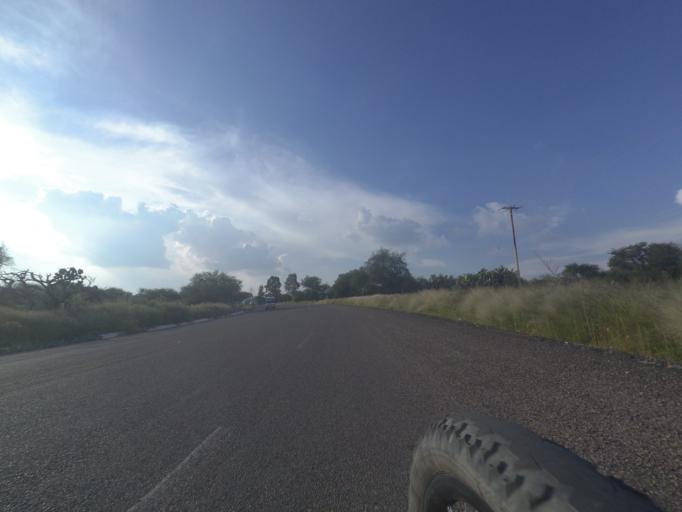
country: MX
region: Aguascalientes
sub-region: Aguascalientes
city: Penuelas (El Cienegal)
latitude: 21.7636
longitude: -102.3519
